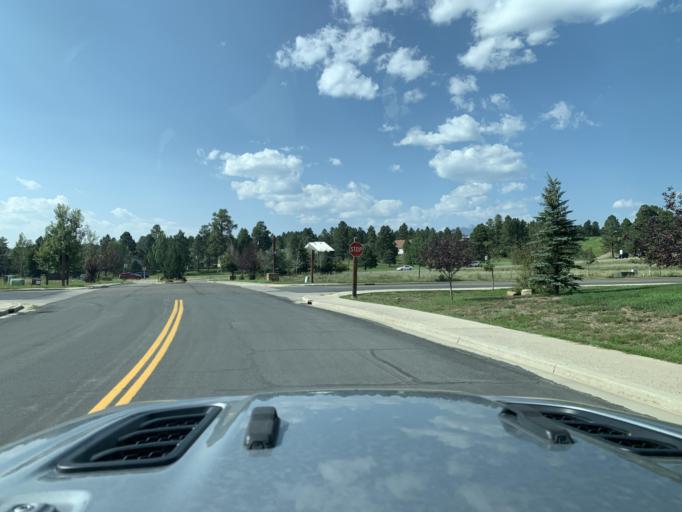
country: US
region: Colorado
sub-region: Archuleta County
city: Pagosa Springs
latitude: 37.2640
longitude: -107.0573
